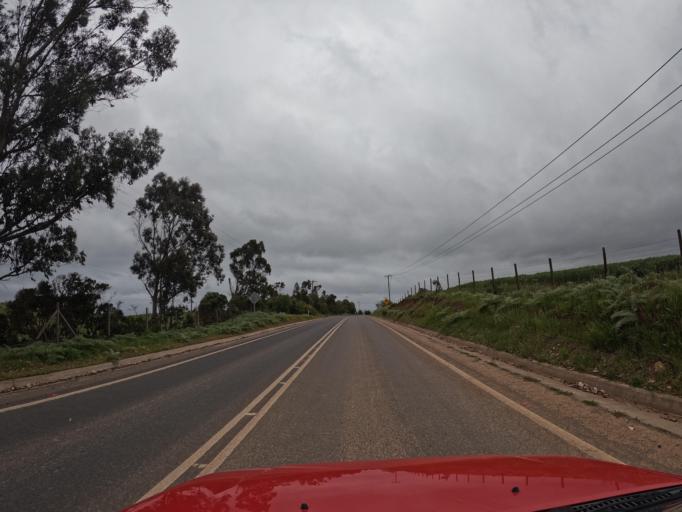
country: CL
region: O'Higgins
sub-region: Provincia de Colchagua
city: Santa Cruz
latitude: -34.4968
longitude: -72.0121
